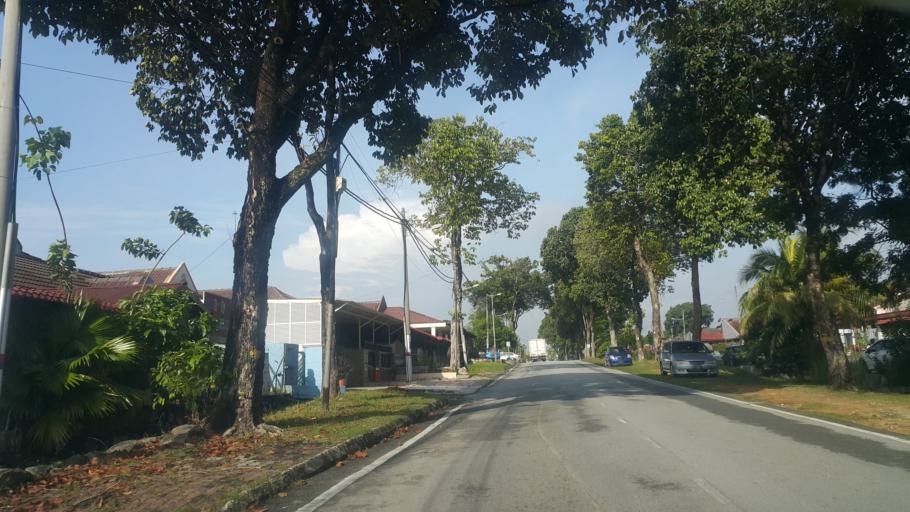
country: MY
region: Selangor
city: Klang
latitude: 3.0123
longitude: 101.4428
